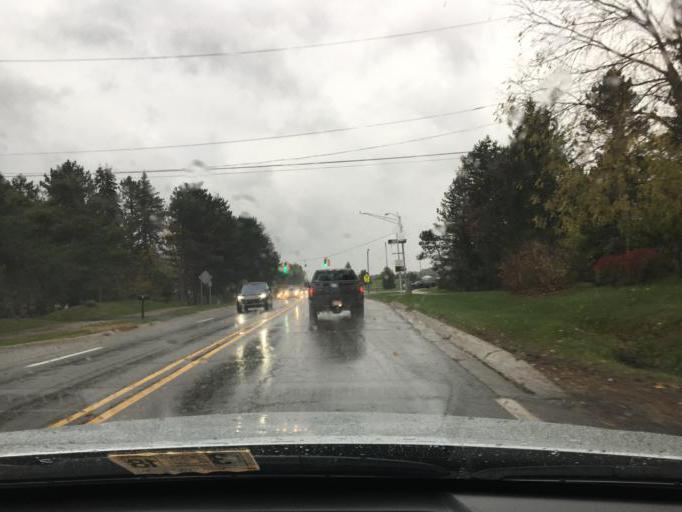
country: US
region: Michigan
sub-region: Oakland County
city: Auburn Hills
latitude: 42.7003
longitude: -83.1949
